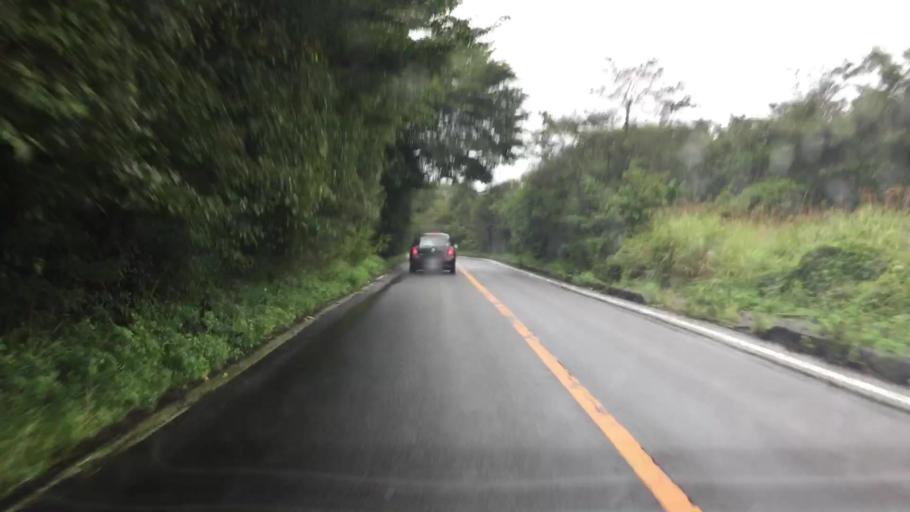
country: JP
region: Yamanashi
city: Fujikawaguchiko
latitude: 35.4055
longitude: 138.6145
